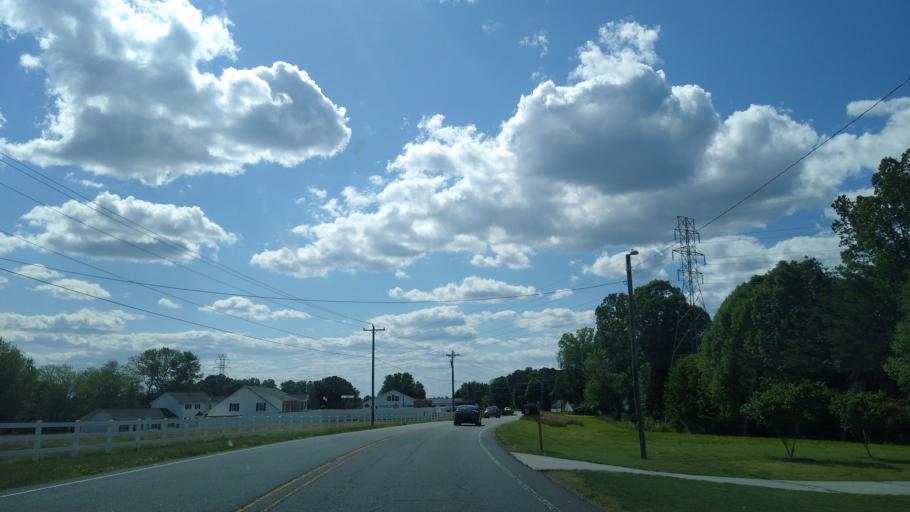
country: US
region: North Carolina
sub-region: Forsyth County
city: Kernersville
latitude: 36.1007
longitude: -80.0861
